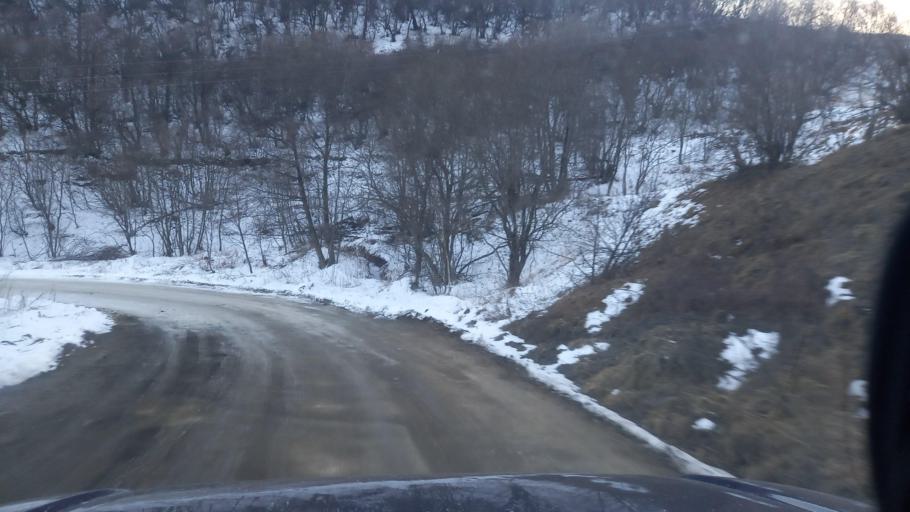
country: RU
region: Ingushetiya
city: Dzhayrakh
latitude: 42.8333
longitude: 44.5679
